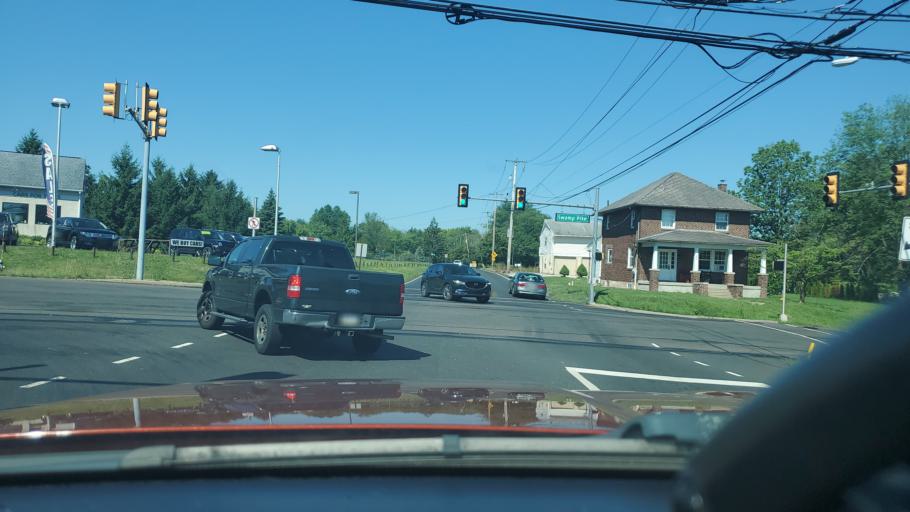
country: US
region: Pennsylvania
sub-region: Montgomery County
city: Limerick
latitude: 40.2474
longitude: -75.5340
